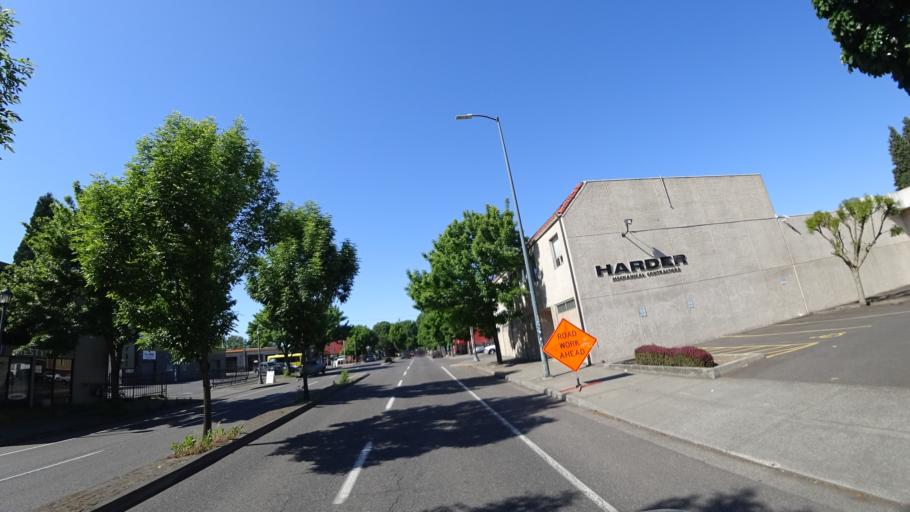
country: US
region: Oregon
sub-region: Multnomah County
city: Portland
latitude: 45.5383
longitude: -122.6616
